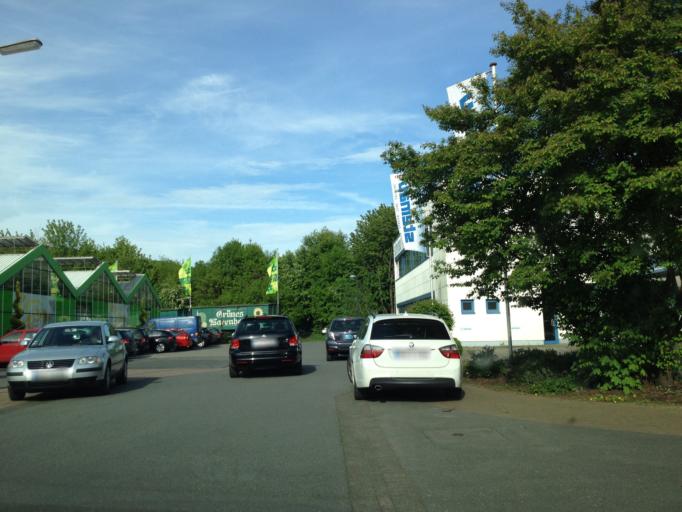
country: DE
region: North Rhine-Westphalia
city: Wickede
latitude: 51.4599
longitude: 7.9519
